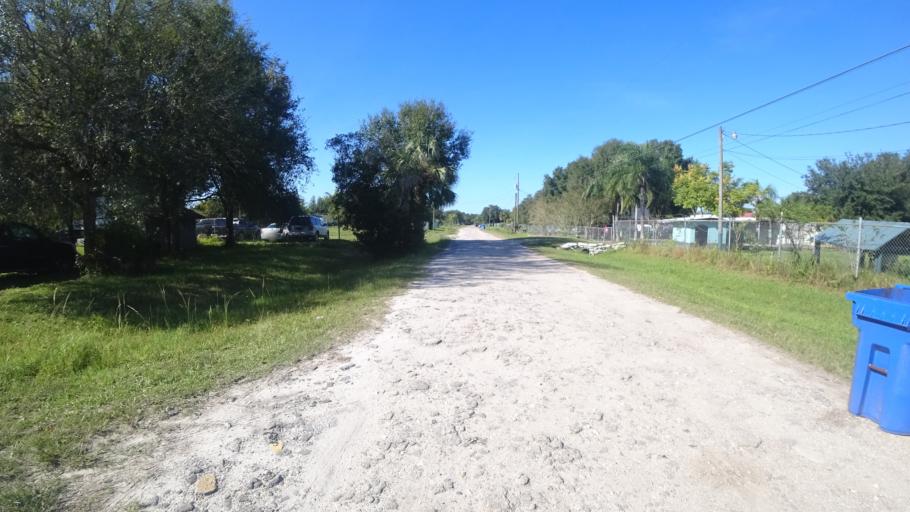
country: US
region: Florida
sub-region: Hillsborough County
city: Sun City Center
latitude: 27.6497
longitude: -82.3551
